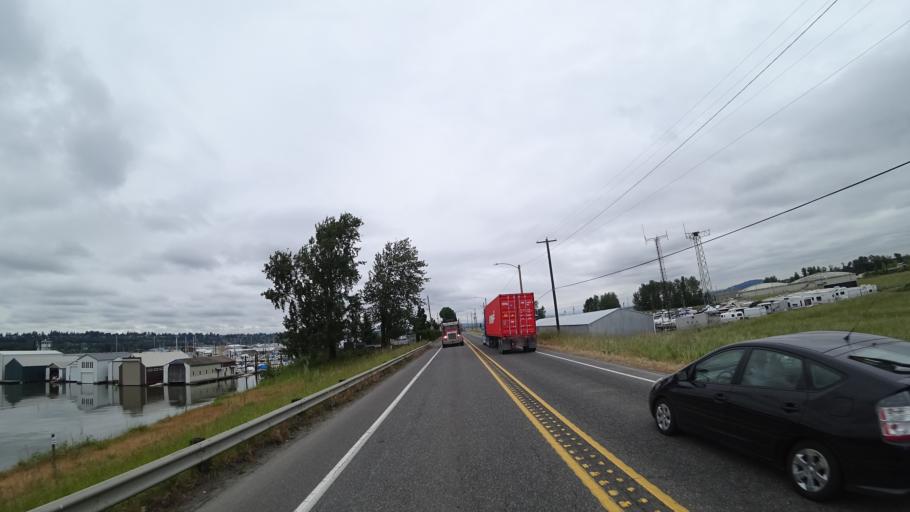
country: US
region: Washington
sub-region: Clark County
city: Vancouver
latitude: 45.6006
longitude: -122.6386
